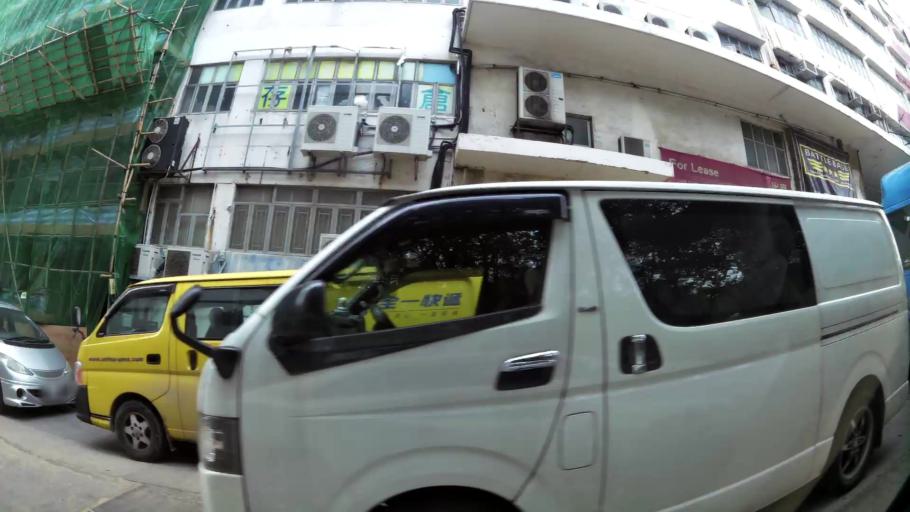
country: HK
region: Kowloon City
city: Kowloon
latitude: 22.2924
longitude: 114.2357
